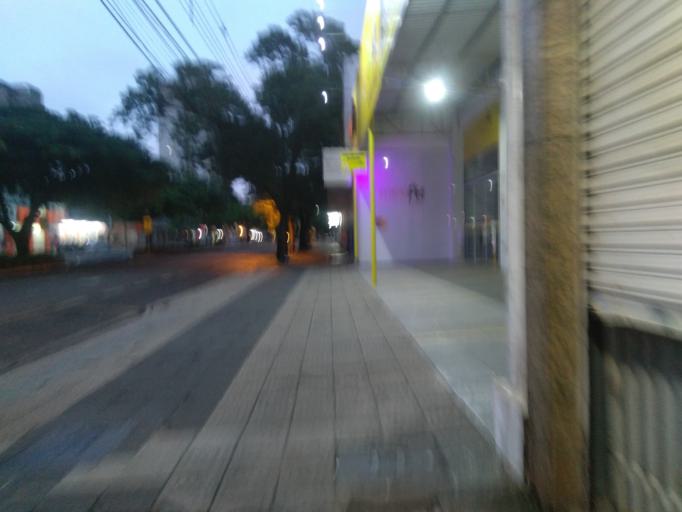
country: BR
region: Parana
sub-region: Maringa
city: Maringa
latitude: -23.4157
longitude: -51.9330
